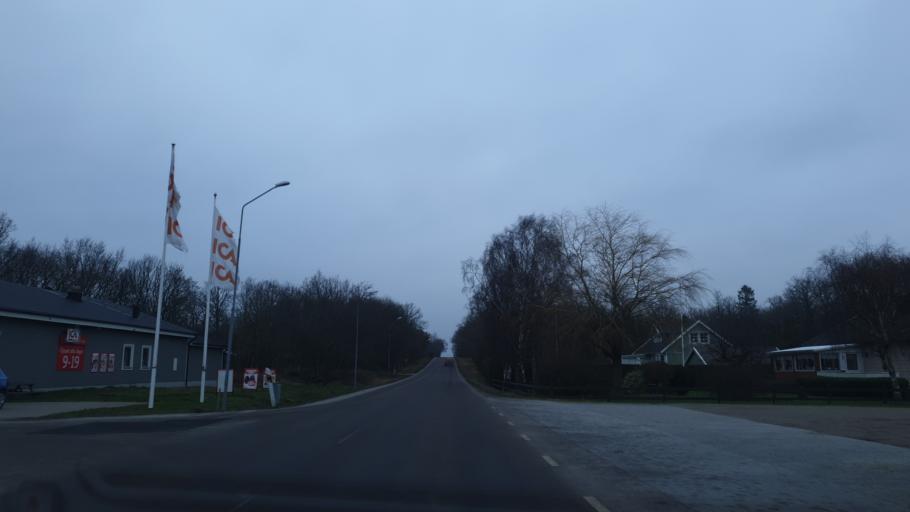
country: SE
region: Blekinge
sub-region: Karlskrona Kommun
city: Sturko
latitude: 56.1254
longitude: 15.7367
